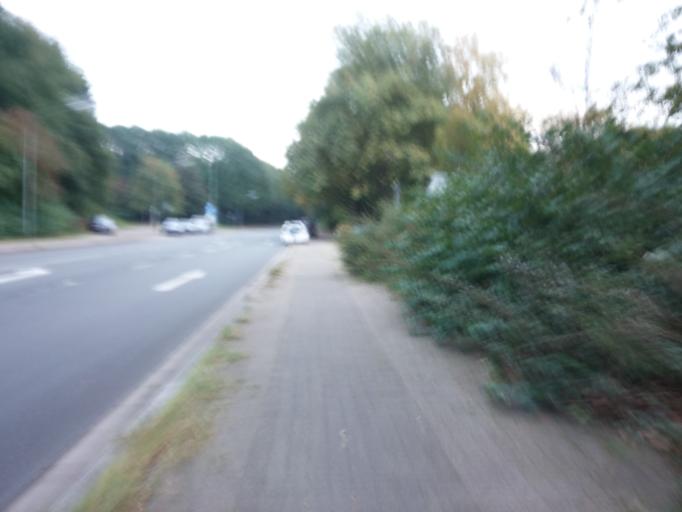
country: DE
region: North Rhine-Westphalia
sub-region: Regierungsbezirk Munster
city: Gladbeck
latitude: 51.6071
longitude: 7.0418
